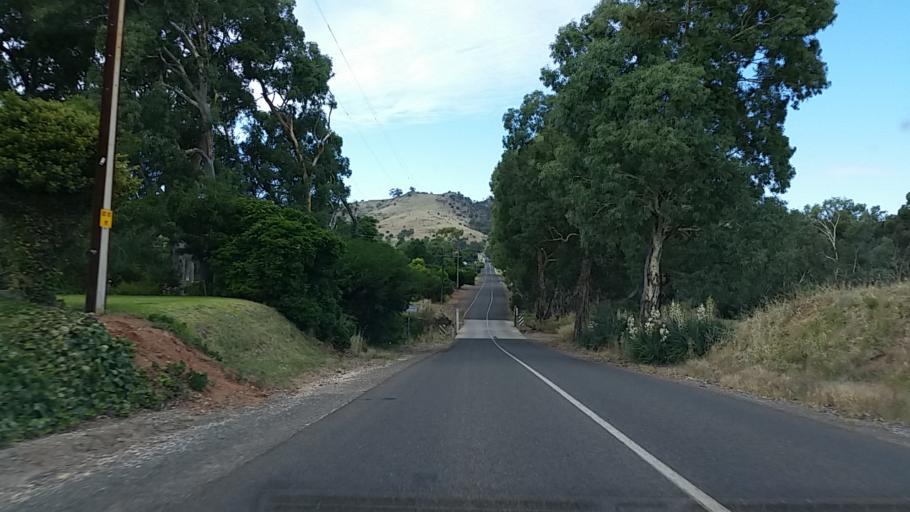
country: AU
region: South Australia
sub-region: Barossa
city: Tanunda
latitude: -34.5413
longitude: 138.9809
